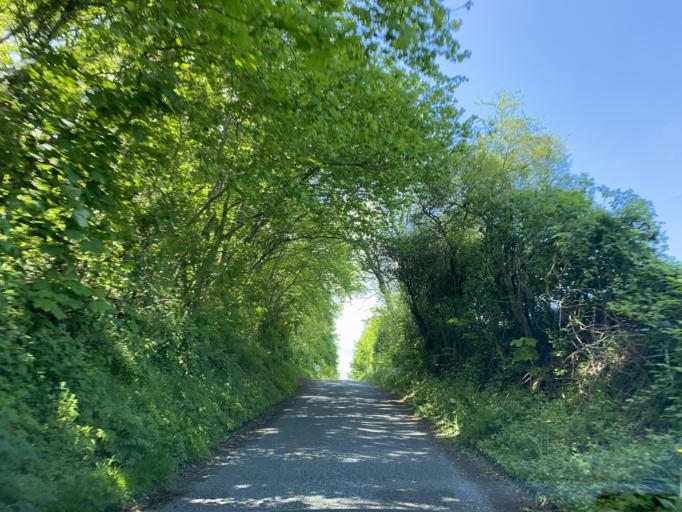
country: DK
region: South Denmark
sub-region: Aabenraa Kommune
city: Lojt Kirkeby
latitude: 55.1232
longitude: 9.4565
